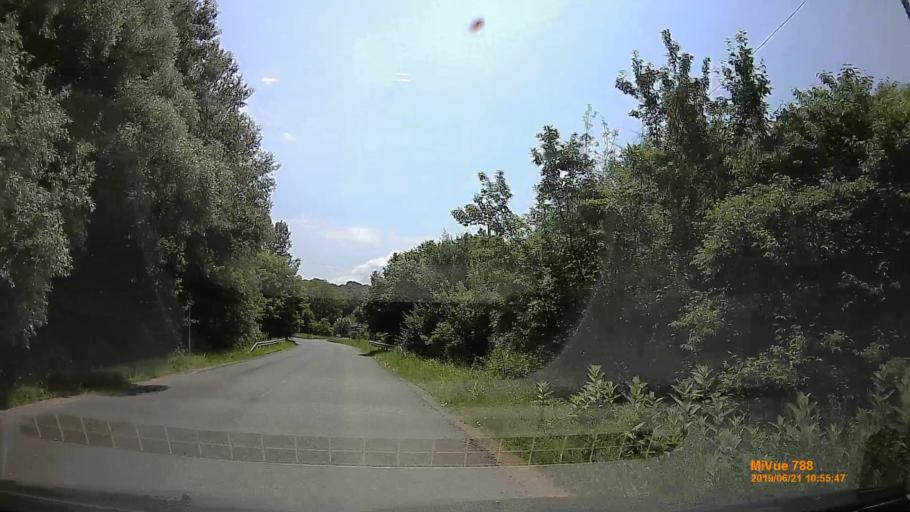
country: HU
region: Baranya
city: Sasd
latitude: 46.1551
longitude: 18.0855
